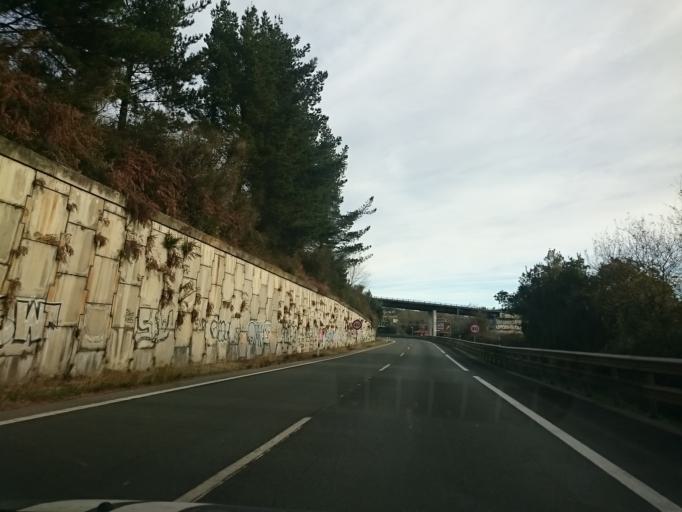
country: ES
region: Asturias
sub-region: Province of Asturias
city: Oviedo
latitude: 43.3300
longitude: -5.8719
